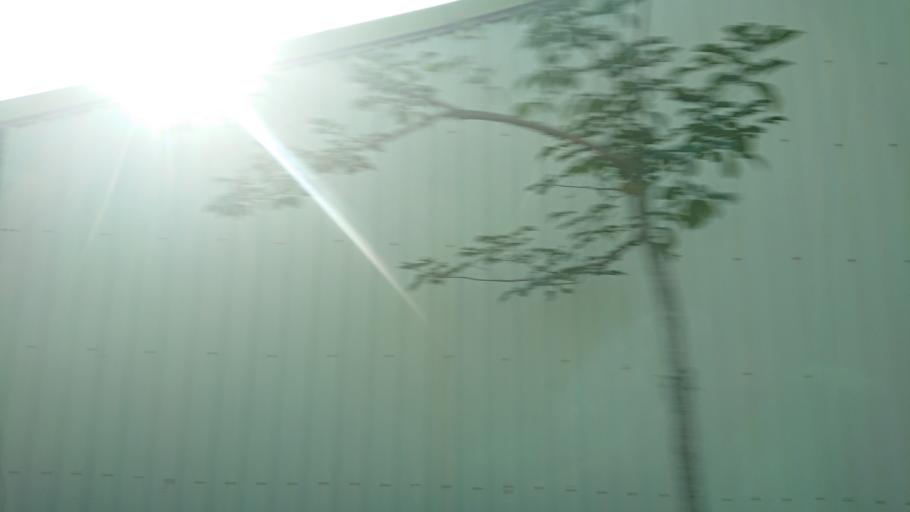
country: TW
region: Taiwan
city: Xinying
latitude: 23.2023
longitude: 120.2712
